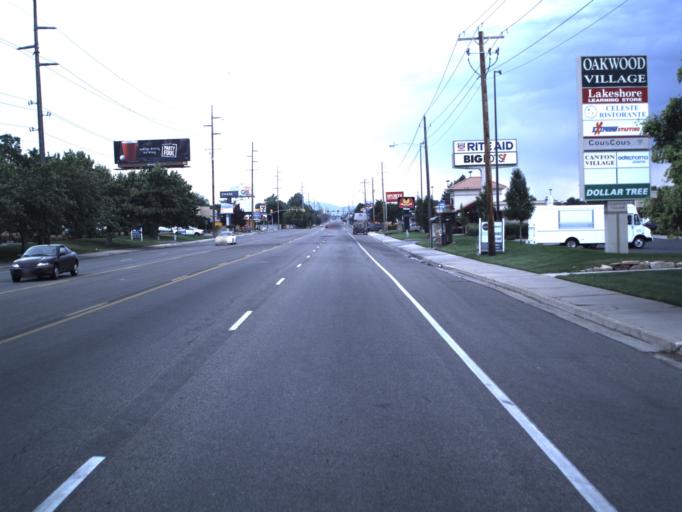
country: US
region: Utah
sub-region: Salt Lake County
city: Murray
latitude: 40.6525
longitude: -111.8660
